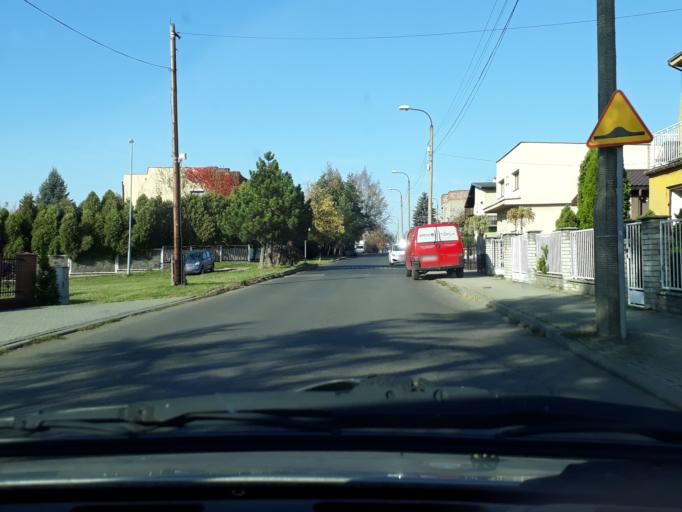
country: PL
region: Silesian Voivodeship
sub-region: Powiat tarnogorski
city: Tarnowskie Gory
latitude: 50.4261
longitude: 18.8740
